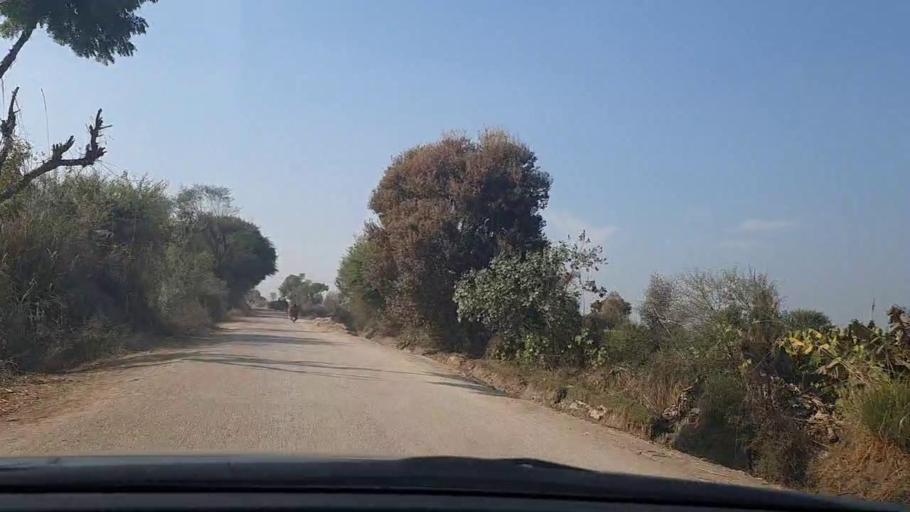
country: PK
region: Sindh
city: Daulatpur
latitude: 26.3067
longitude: 68.0857
